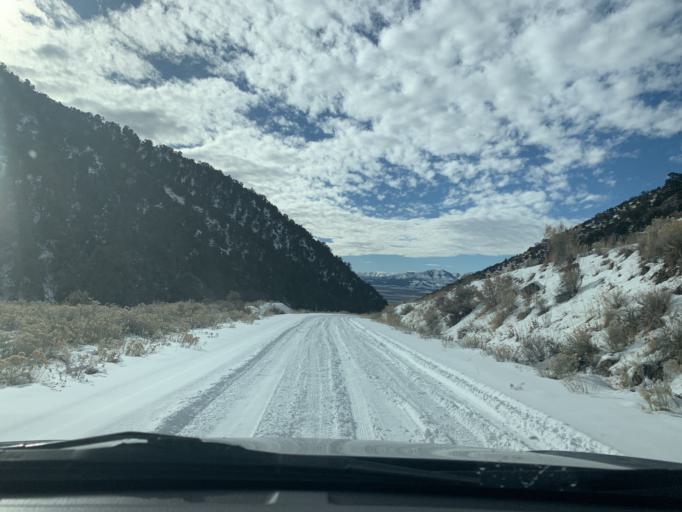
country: US
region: Utah
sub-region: Utah County
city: Eagle Mountain
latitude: 40.3153
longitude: -112.2319
